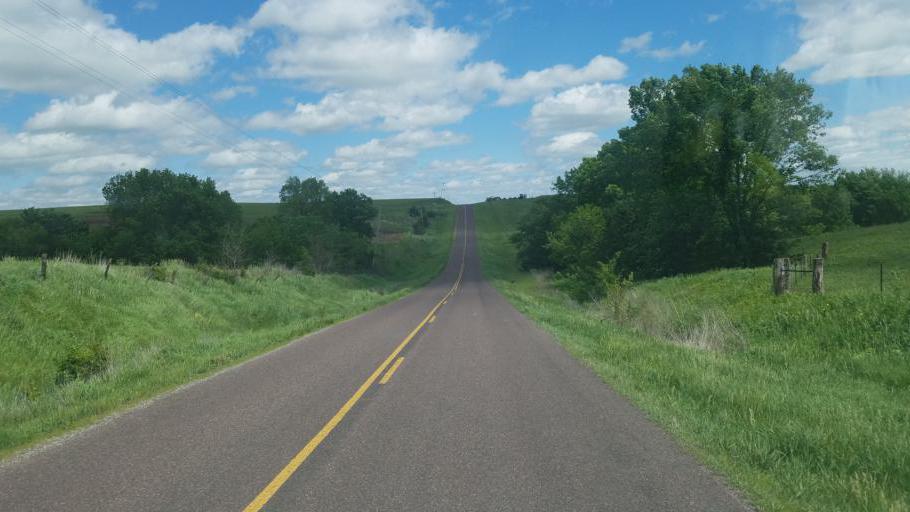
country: US
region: Iowa
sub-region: Decatur County
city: Lamoni
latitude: 40.4713
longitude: -94.0546
